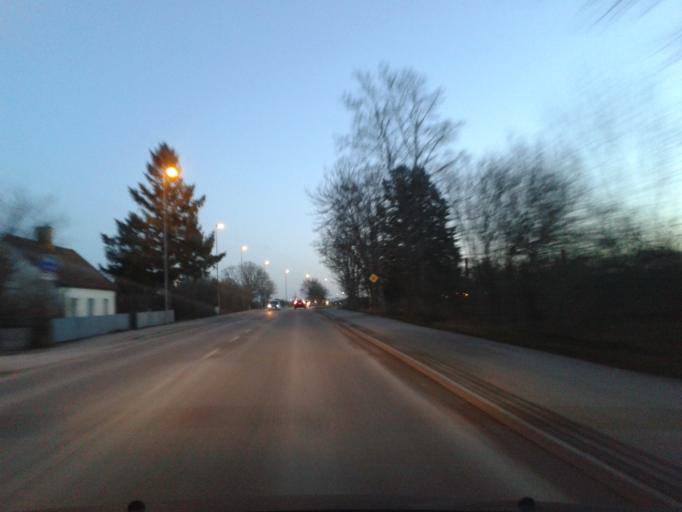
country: SE
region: Gotland
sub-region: Gotland
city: Visby
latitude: 57.6293
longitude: 18.3158
